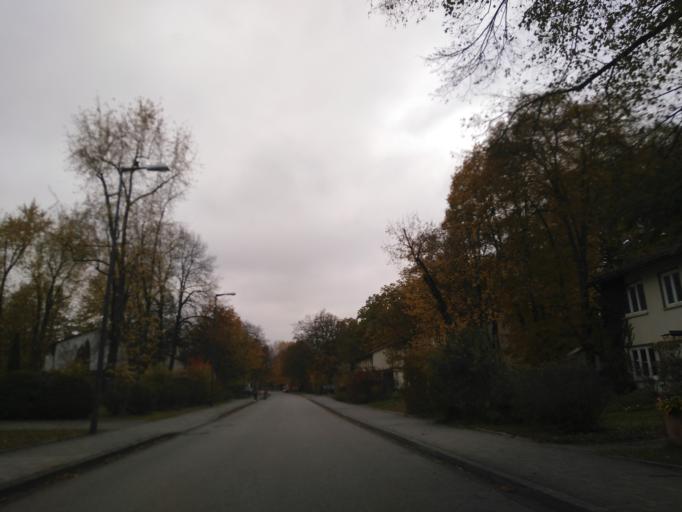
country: DE
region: Bavaria
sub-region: Upper Bavaria
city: Unterhaching
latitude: 48.0894
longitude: 11.6034
